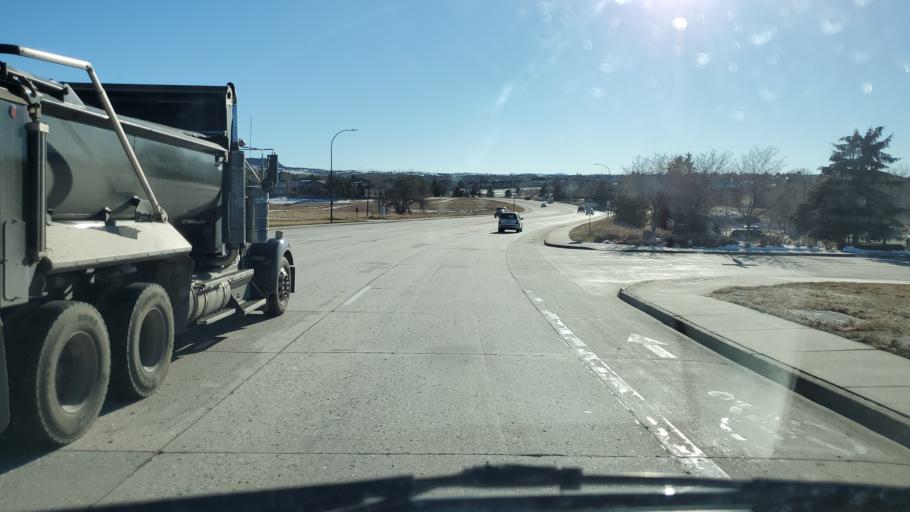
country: US
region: Colorado
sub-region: Douglas County
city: Carriage Club
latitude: 39.5390
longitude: -104.9156
